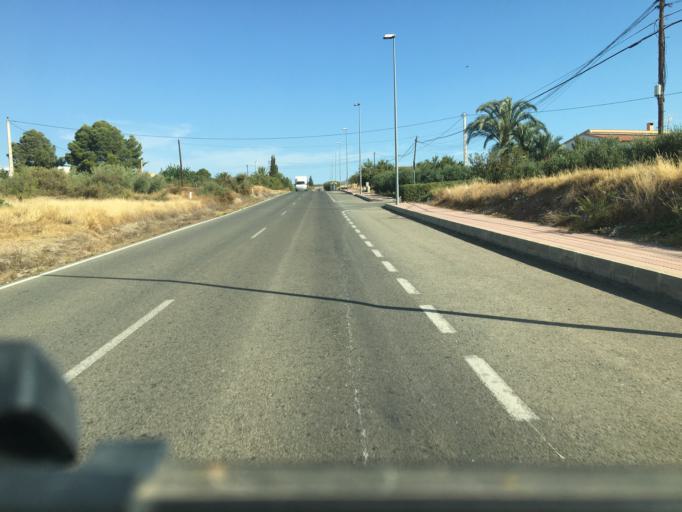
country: ES
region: Andalusia
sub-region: Provincia de Almeria
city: Huercal-Overa
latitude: 37.4485
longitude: -1.9843
